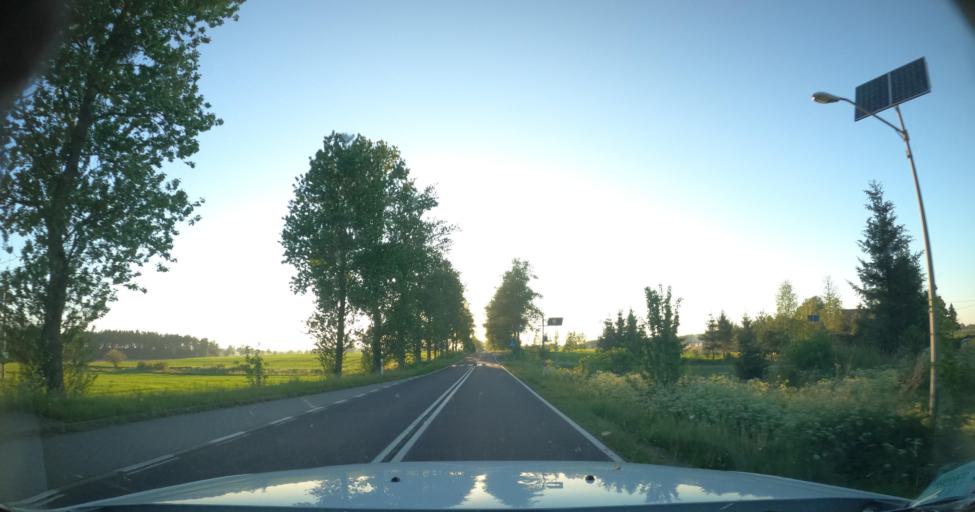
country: PL
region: Pomeranian Voivodeship
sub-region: Powiat slupski
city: Damnica
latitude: 54.4338
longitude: 17.3558
